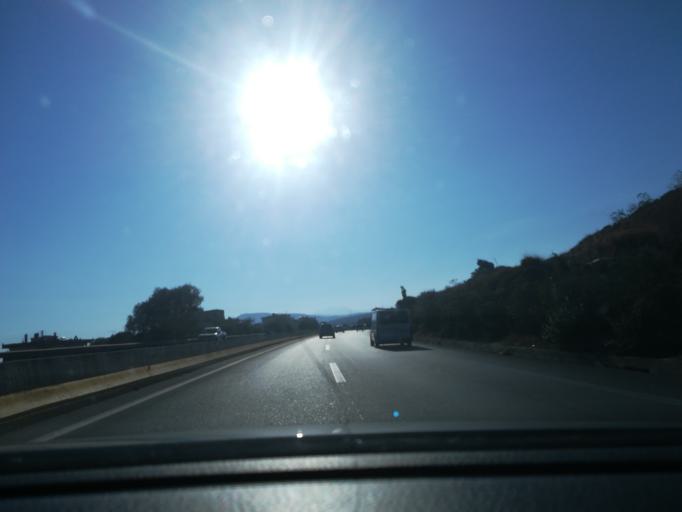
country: GR
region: Crete
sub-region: Nomos Irakleiou
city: Gournes
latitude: 35.3277
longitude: 25.2720
